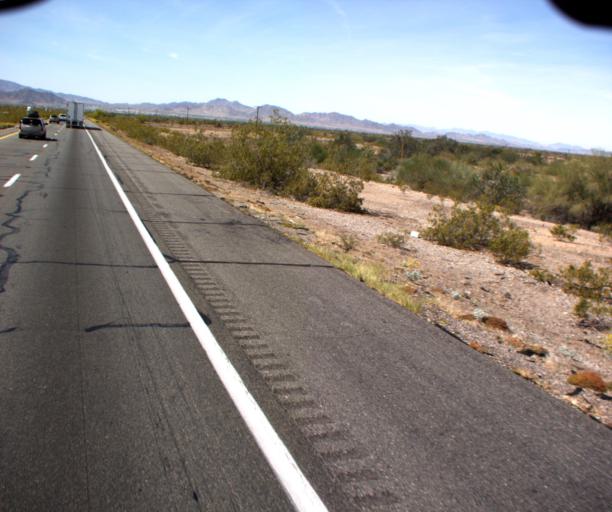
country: US
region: Arizona
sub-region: La Paz County
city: Quartzsite
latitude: 33.6739
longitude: -114.1388
